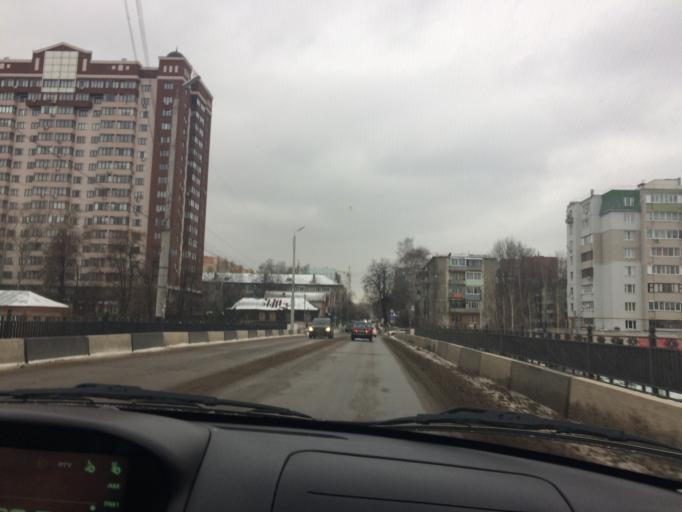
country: RU
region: Rjazan
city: Ryazan'
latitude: 54.6208
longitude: 39.7401
